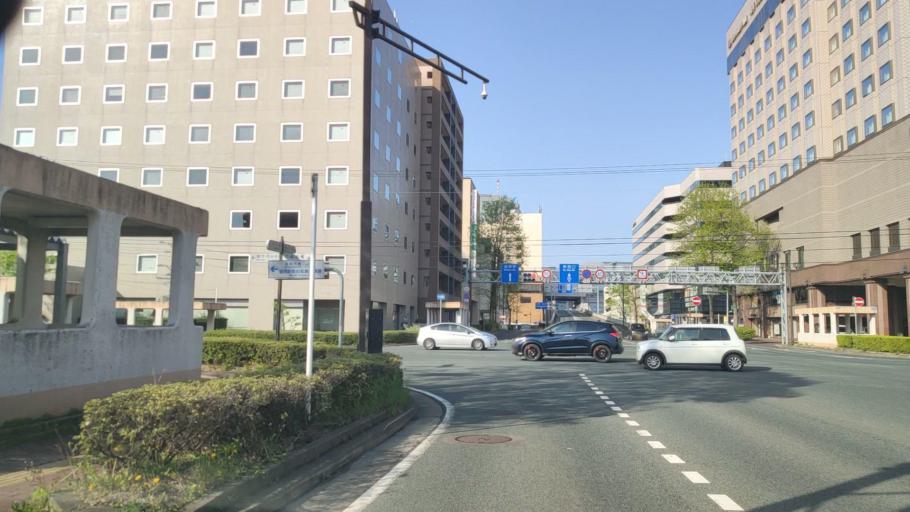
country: JP
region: Iwate
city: Morioka-shi
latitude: 39.7045
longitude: 141.1377
